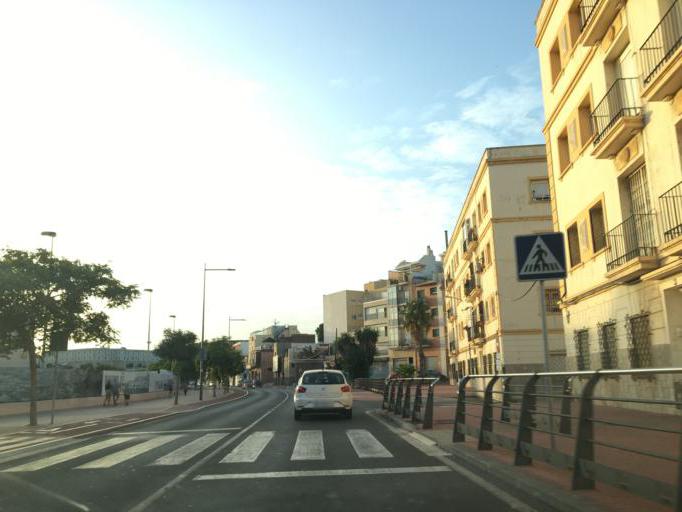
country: ES
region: Murcia
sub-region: Murcia
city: Cartagena
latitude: 37.5980
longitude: -0.9733
